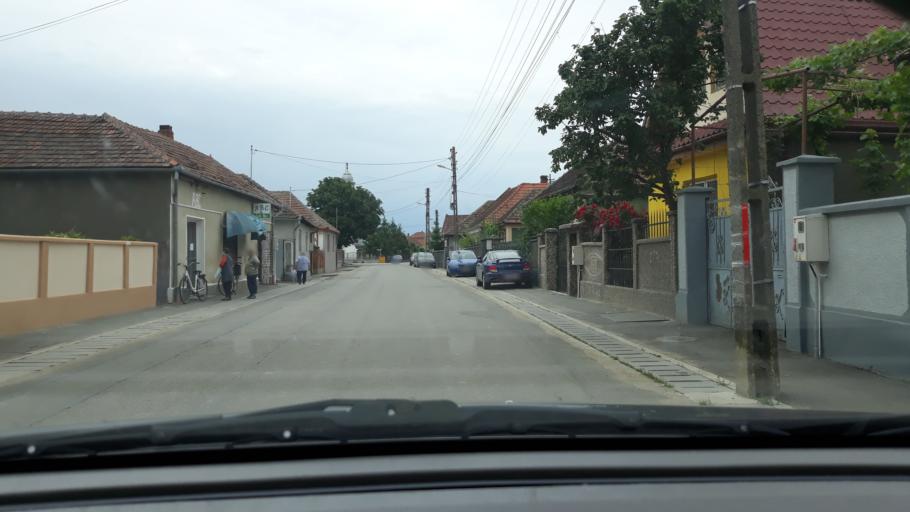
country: RO
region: Bihor
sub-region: Comuna Osorheiu
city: Osorheiu
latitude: 47.0578
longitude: 22.0439
